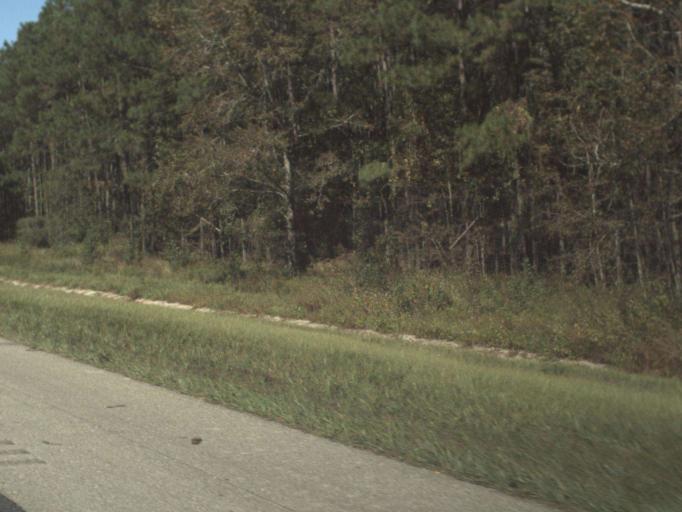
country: US
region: Florida
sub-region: Washington County
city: Chipley
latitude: 30.7457
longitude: -85.4720
